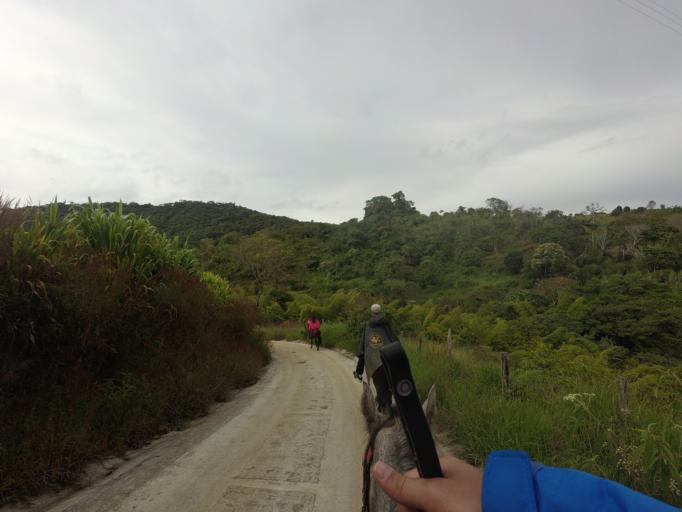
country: CO
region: Huila
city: San Agustin
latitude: 1.9079
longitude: -76.2939
